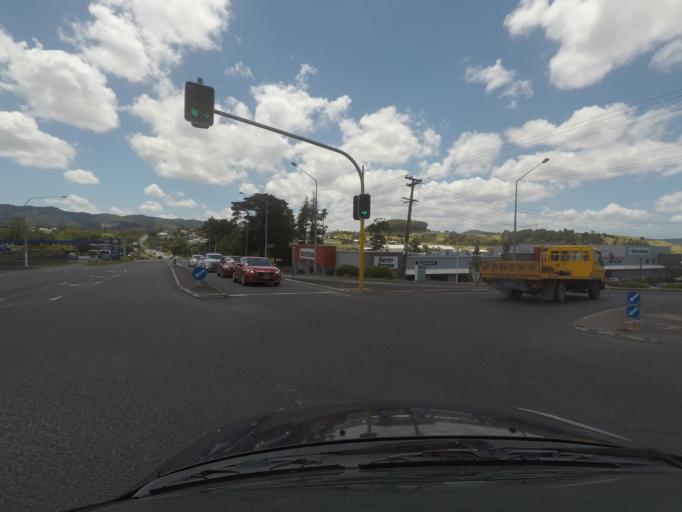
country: NZ
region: Northland
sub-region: Whangarei
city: Whangarei
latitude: -35.7525
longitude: 174.3096
